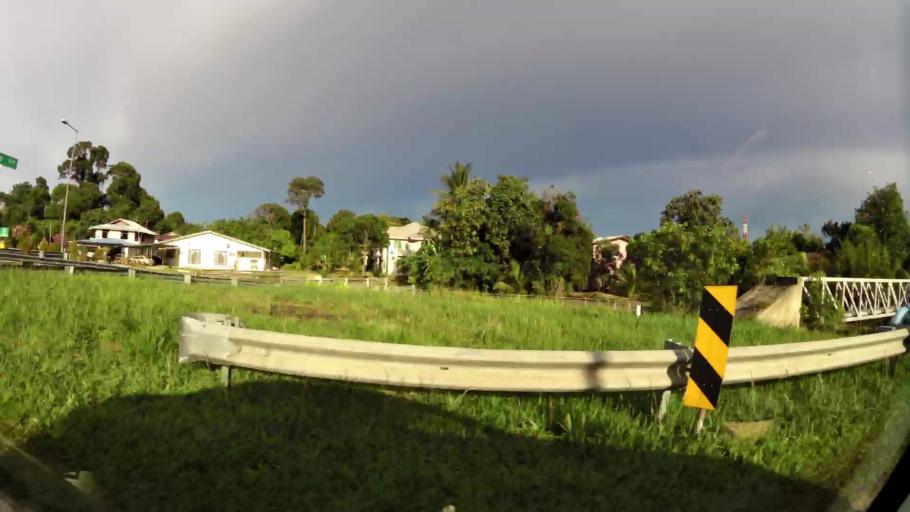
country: BN
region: Brunei and Muara
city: Bandar Seri Begawan
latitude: 4.9620
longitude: 115.0203
